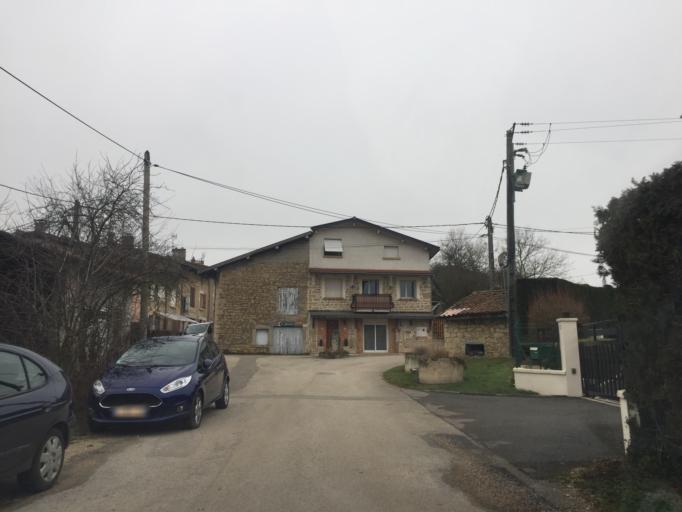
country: FR
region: Rhone-Alpes
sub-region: Departement de l'Ain
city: Ambronay
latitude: 45.9929
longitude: 5.3434
